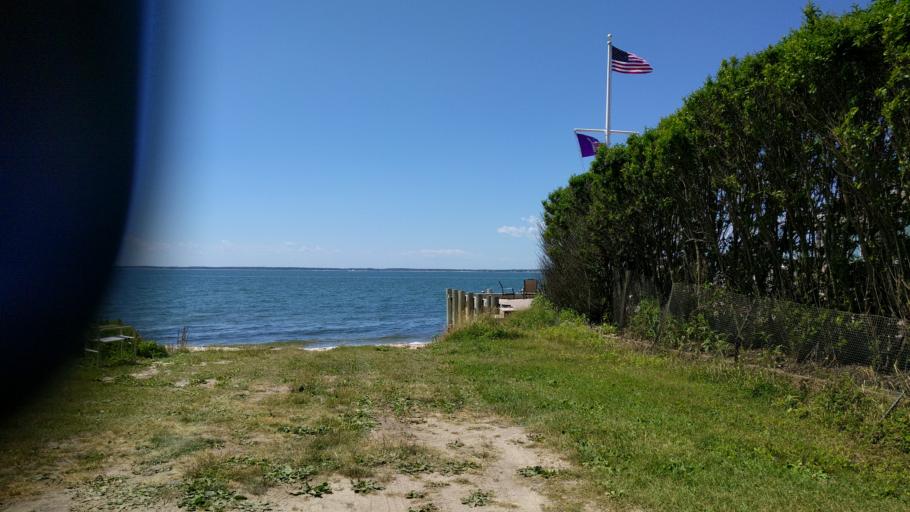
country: US
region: New York
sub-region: Suffolk County
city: Noyack
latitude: 40.9864
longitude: -72.3757
